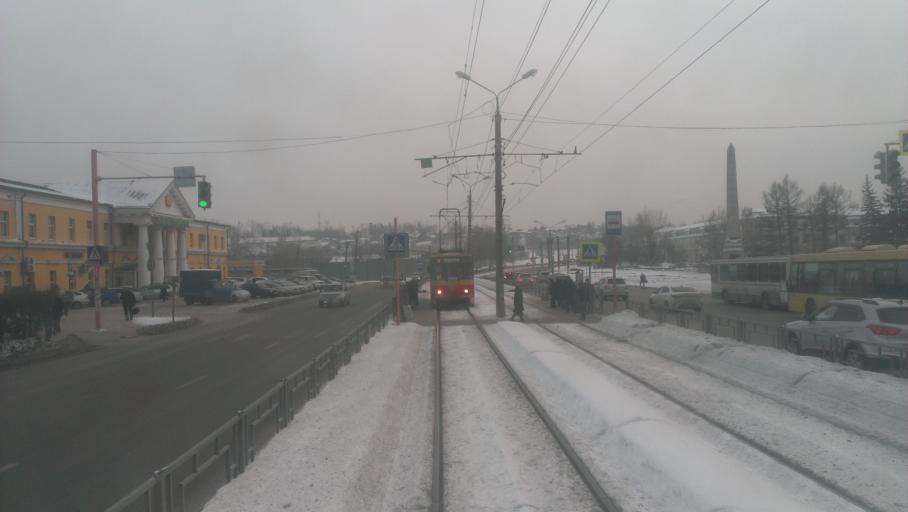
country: RU
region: Altai Krai
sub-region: Gorod Barnaulskiy
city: Barnaul
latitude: 53.3295
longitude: 83.7841
